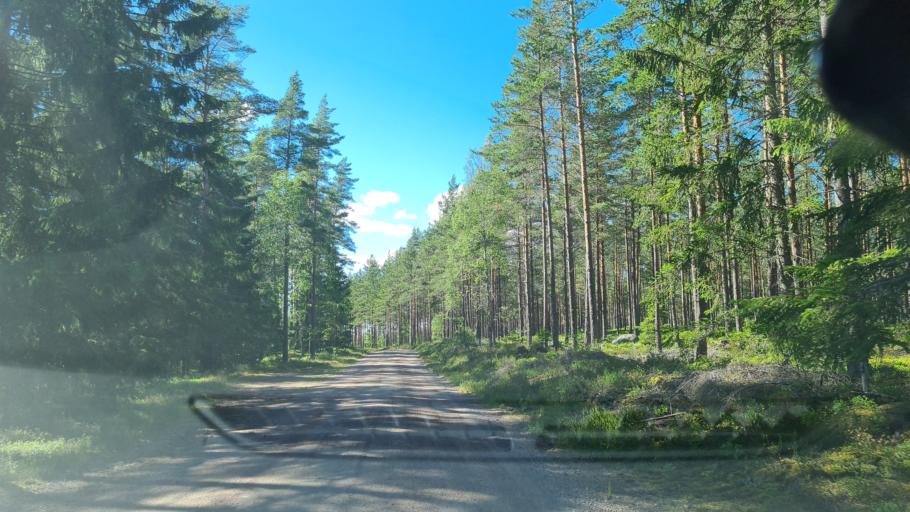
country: SE
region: OEstergoetland
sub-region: Norrkopings Kommun
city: Krokek
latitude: 58.6926
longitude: 16.4316
